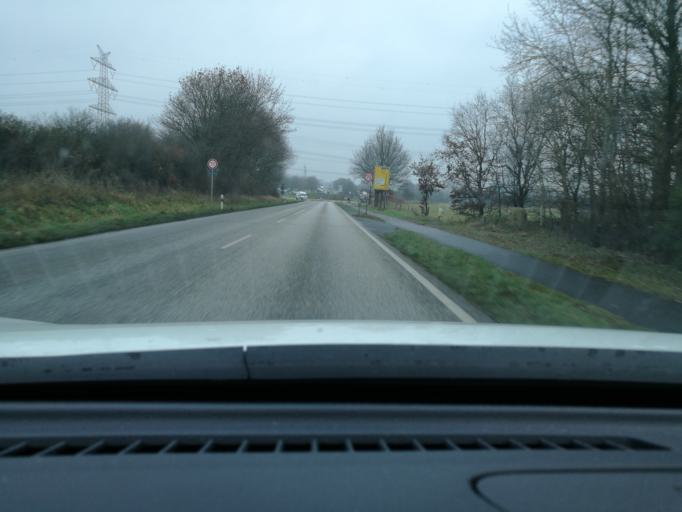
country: DE
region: Schleswig-Holstein
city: Borgstedt
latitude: 54.3405
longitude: 9.6981
